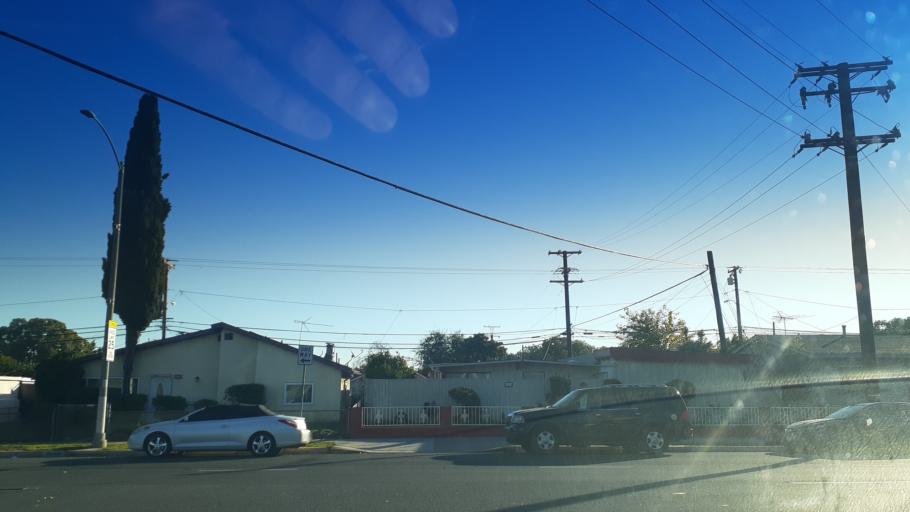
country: US
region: California
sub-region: Los Angeles County
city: Hawaiian Gardens
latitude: 33.8432
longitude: -118.0821
